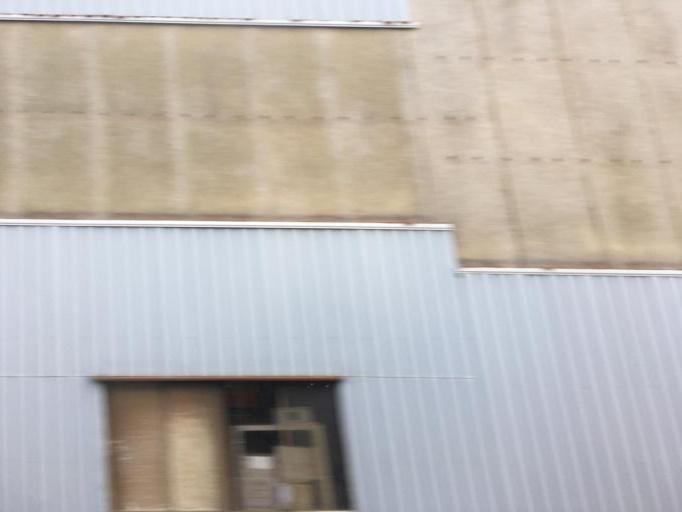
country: JP
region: Tochigi
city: Sano
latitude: 36.3185
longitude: 139.5985
